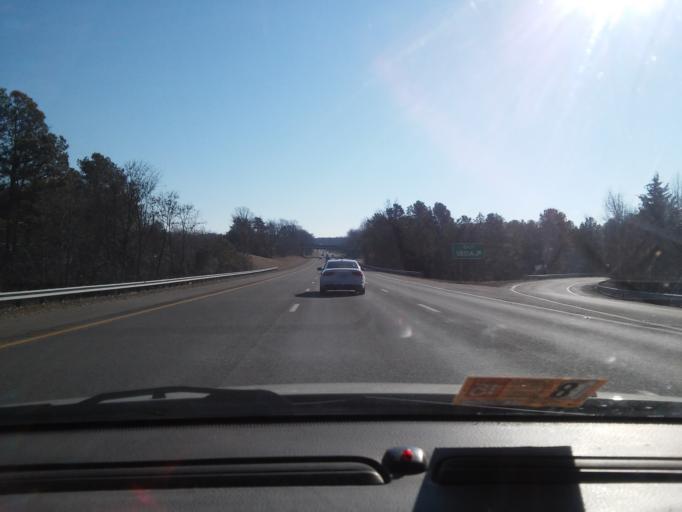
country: US
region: Virginia
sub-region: Henrico County
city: Short Pump
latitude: 37.6369
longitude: -77.5783
